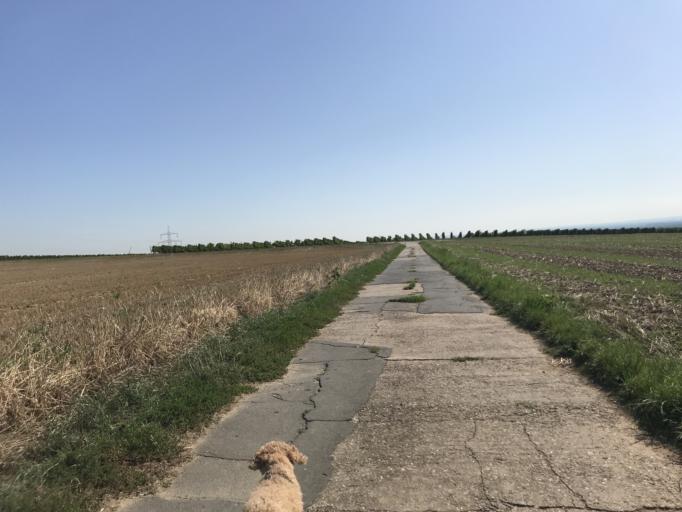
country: DE
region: Rheinland-Pfalz
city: Bodenheim
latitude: 49.9496
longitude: 8.2950
